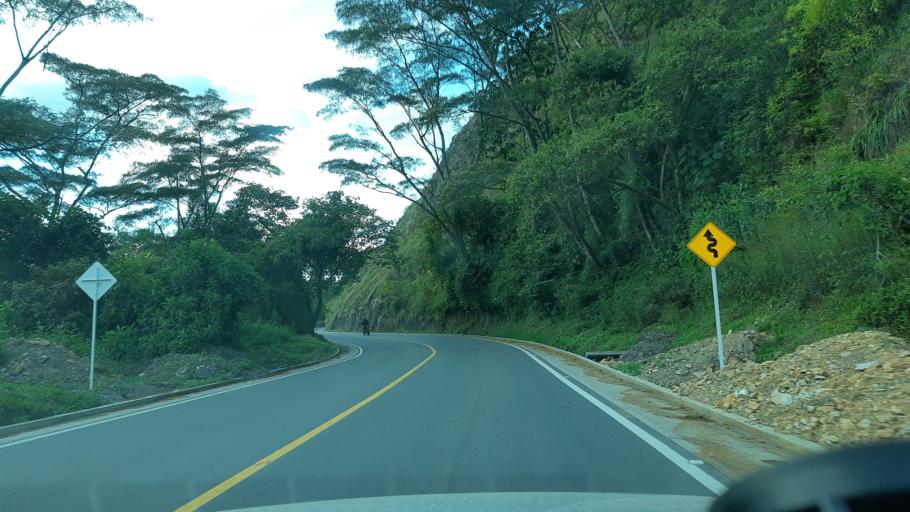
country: CO
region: Boyaca
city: Somondoco
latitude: 4.9904
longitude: -73.3502
